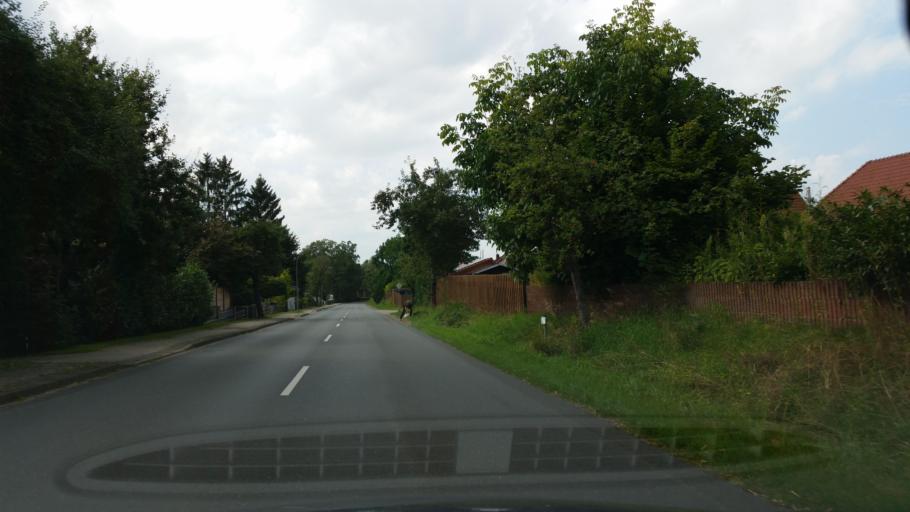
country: DE
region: Lower Saxony
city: Neuenkirchen
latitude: 53.0374
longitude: 9.7152
